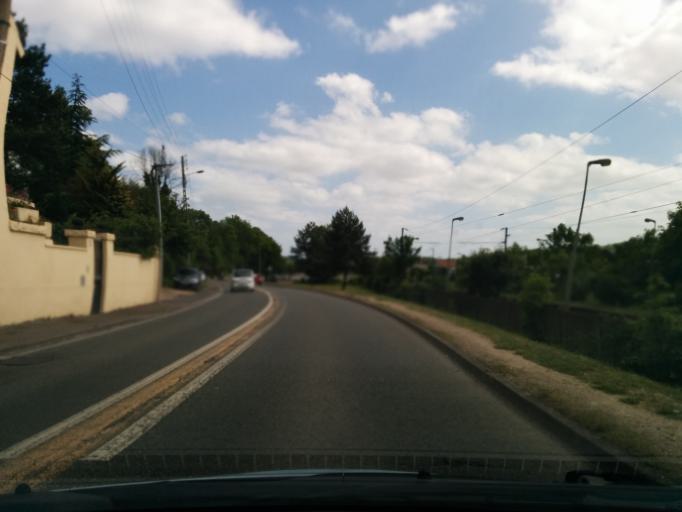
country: FR
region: Ile-de-France
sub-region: Departement des Yvelines
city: Aulnay-sur-Mauldre
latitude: 48.9402
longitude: 1.8400
